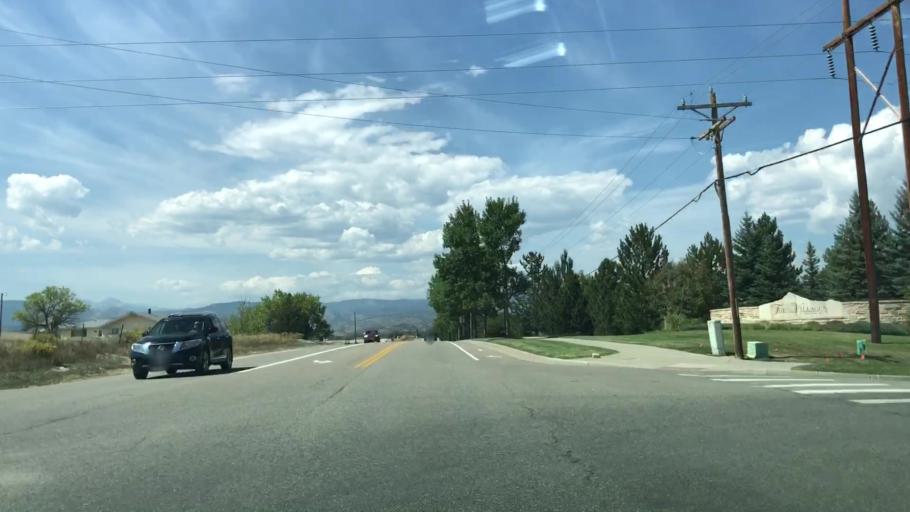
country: US
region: Colorado
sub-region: Larimer County
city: Loveland
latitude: 40.3929
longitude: -105.1313
